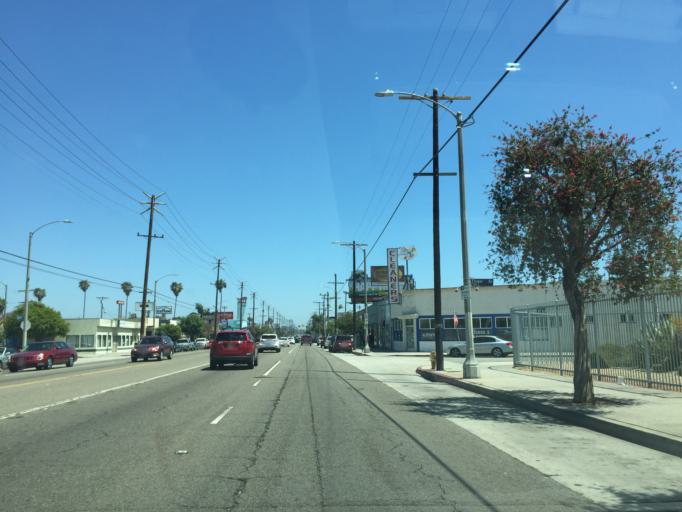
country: US
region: California
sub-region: Los Angeles County
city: Marina del Rey
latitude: 34.0010
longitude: -118.4673
